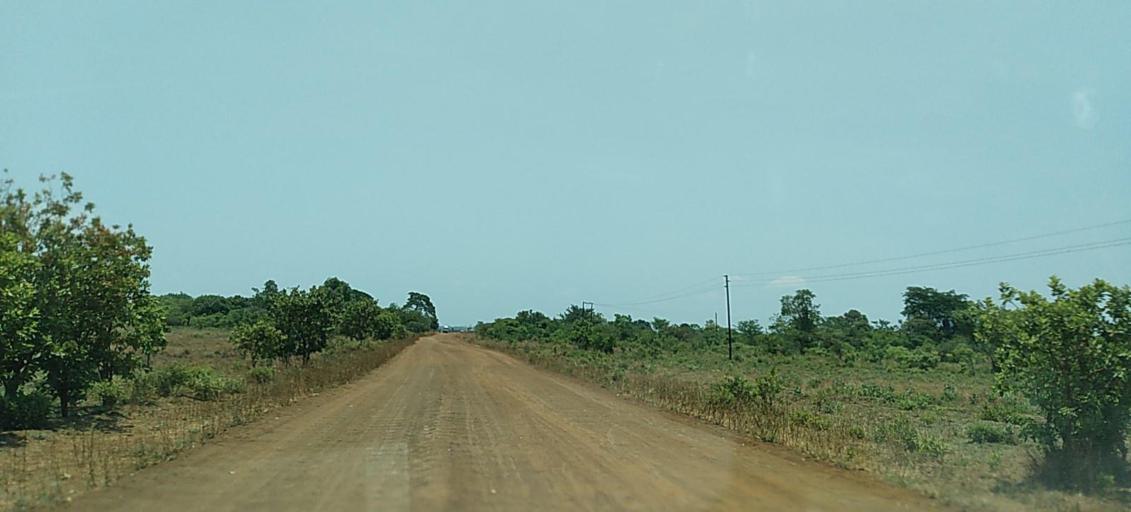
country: ZM
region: Copperbelt
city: Mpongwe
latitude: -13.6780
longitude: 27.8570
